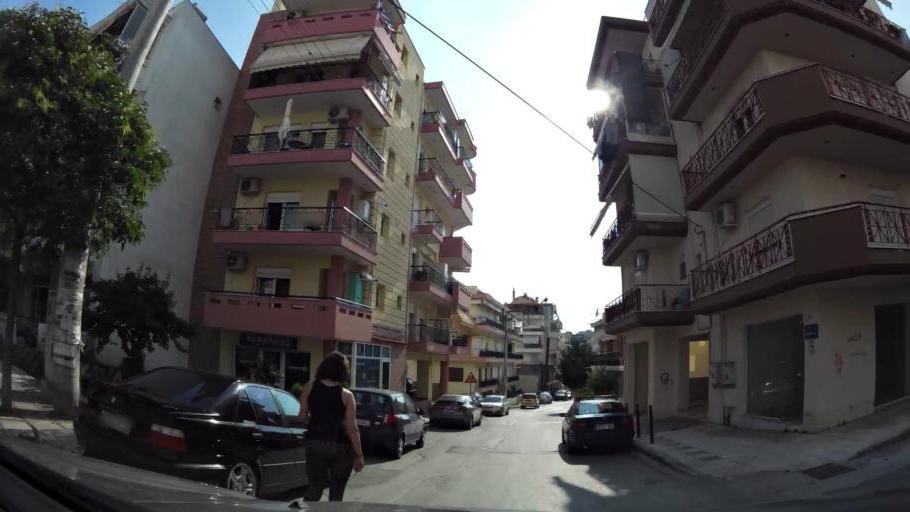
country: GR
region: Central Macedonia
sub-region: Nomos Thessalonikis
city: Sykies
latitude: 40.6557
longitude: 22.9563
